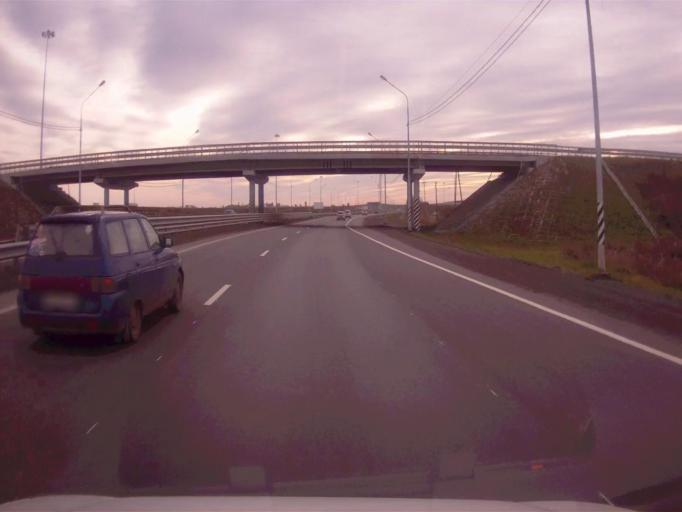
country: RU
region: Chelyabinsk
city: Novosineglazovskiy
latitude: 55.0025
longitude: 61.4539
